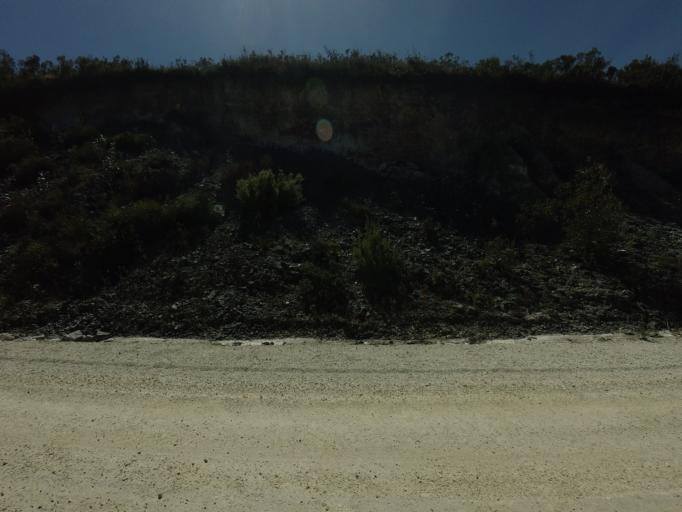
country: AU
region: Tasmania
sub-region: Huon Valley
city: Geeveston
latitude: -42.9336
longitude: 146.3456
